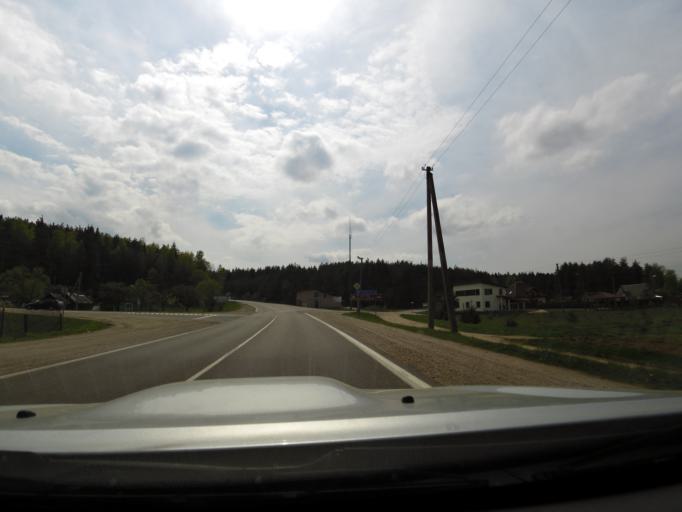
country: LT
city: Salcininkai
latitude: 54.4353
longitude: 25.3254
